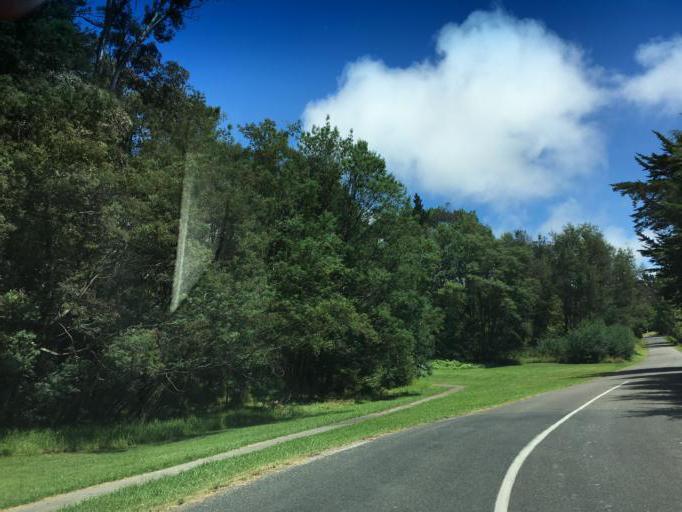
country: NZ
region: Hawke's Bay
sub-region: Wairoa District
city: Wairoa
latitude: -39.0449
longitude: 177.4165
